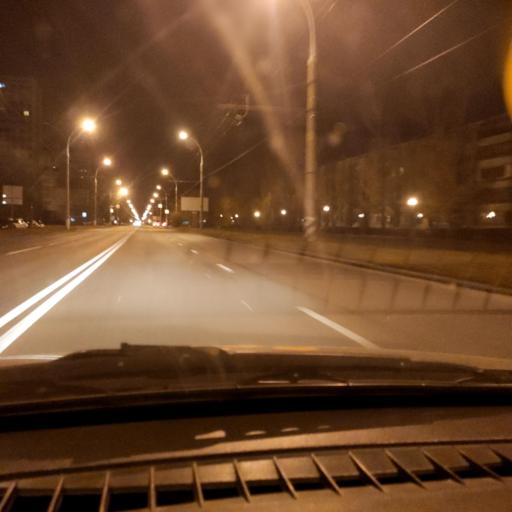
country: RU
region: Samara
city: Tol'yatti
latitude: 53.5054
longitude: 49.2906
